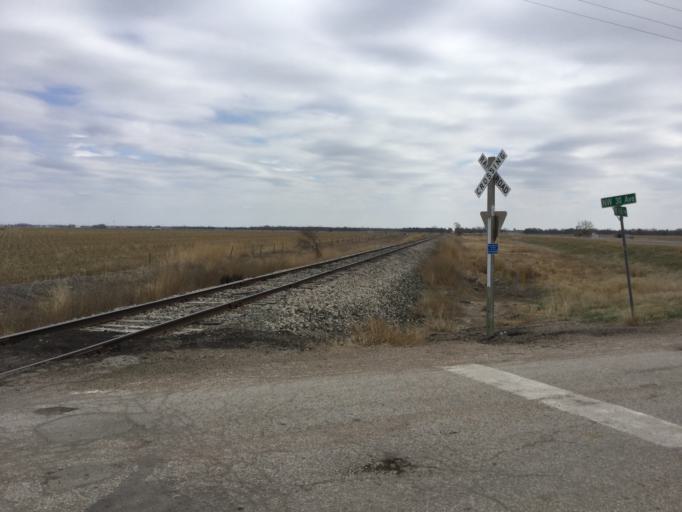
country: US
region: Kansas
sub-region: Barton County
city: Great Bend
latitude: 38.3896
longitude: -98.8300
